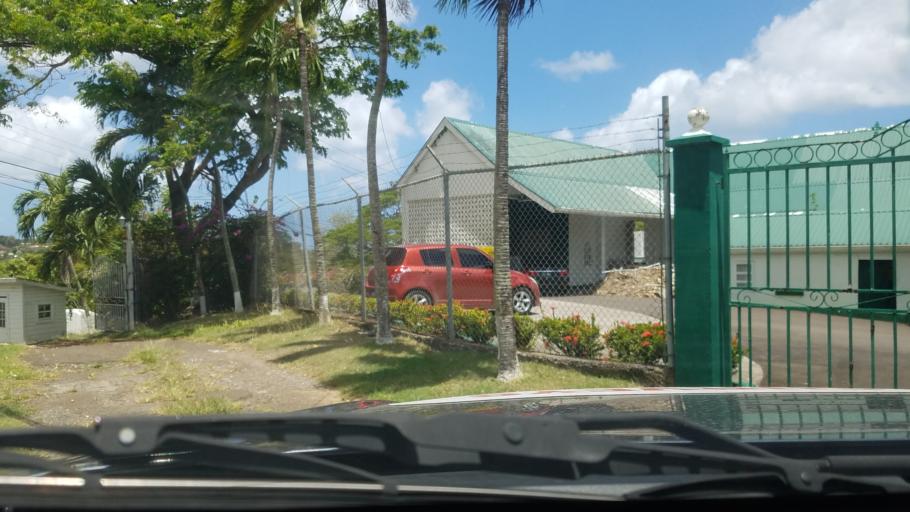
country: LC
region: Castries Quarter
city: Bisee
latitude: 14.0182
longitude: -60.9944
